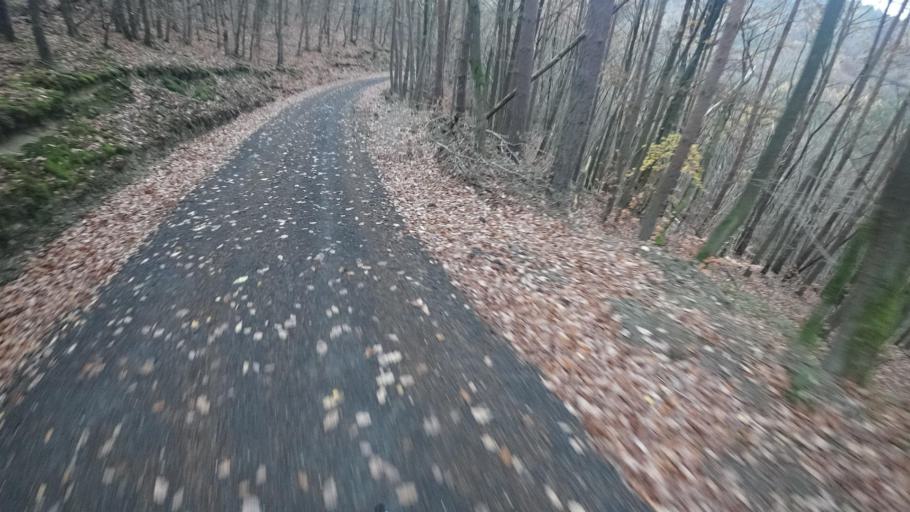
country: DE
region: Rheinland-Pfalz
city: Rech
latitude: 50.5044
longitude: 7.0470
